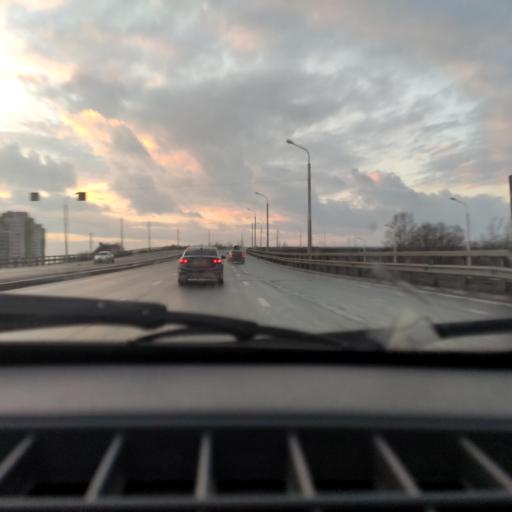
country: RU
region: Bashkortostan
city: Mikhaylovka
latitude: 54.7009
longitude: 55.8640
